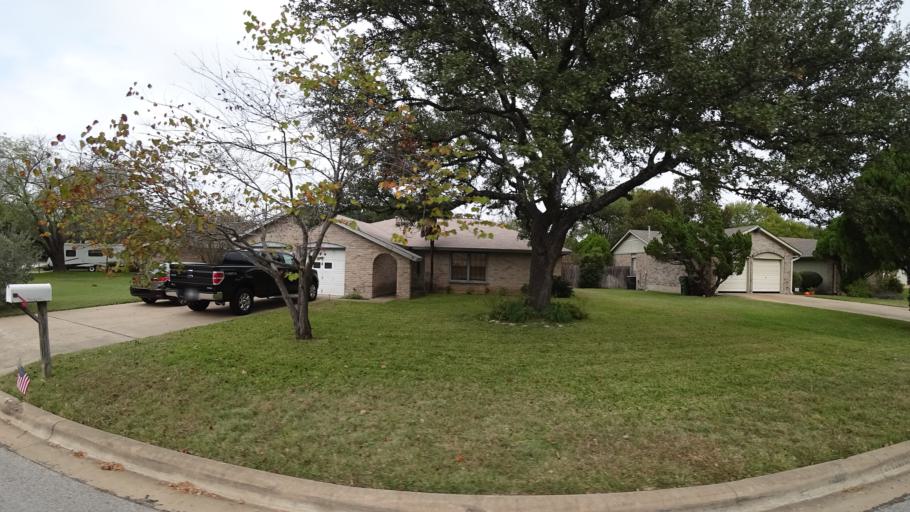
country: US
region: Texas
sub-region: Williamson County
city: Round Rock
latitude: 30.4900
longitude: -97.7010
